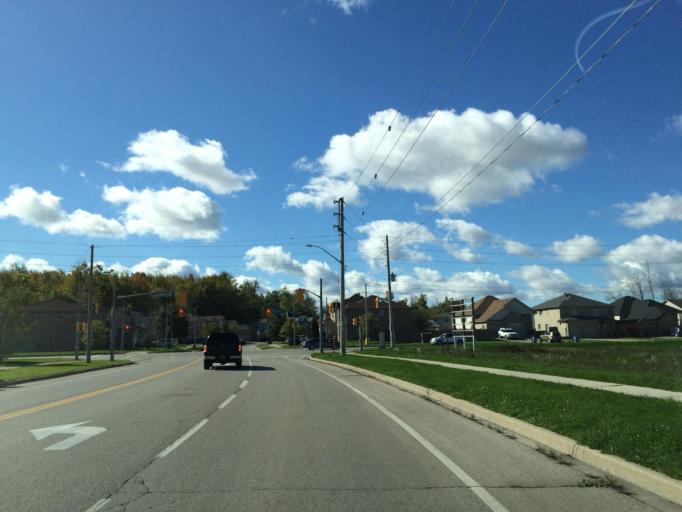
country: CA
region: Ontario
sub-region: Wellington County
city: Guelph
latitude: 43.5272
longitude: -80.2976
